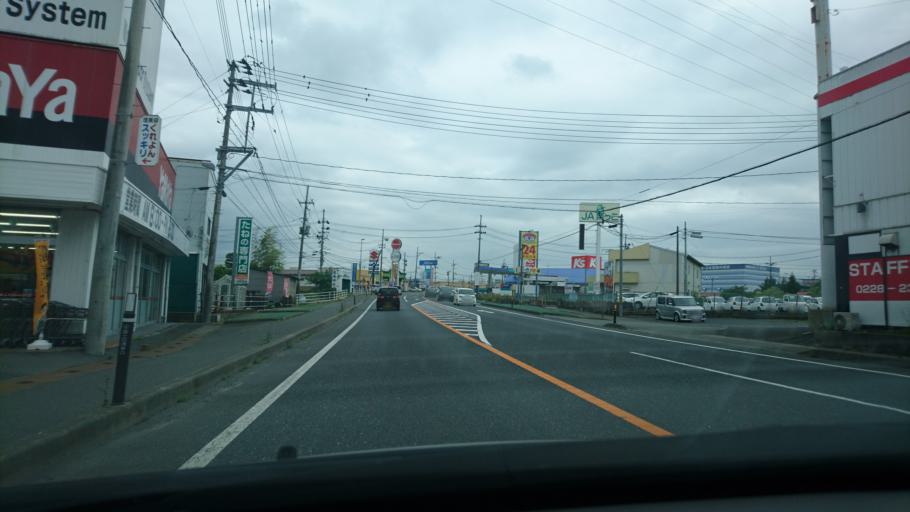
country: JP
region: Miyagi
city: Furukawa
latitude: 38.7386
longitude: 141.0209
